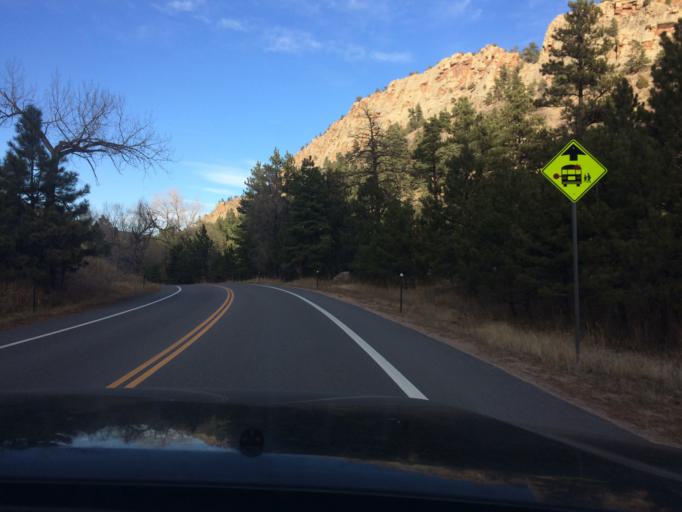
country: US
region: Colorado
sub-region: Boulder County
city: Boulder
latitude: 40.1161
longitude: -105.3072
